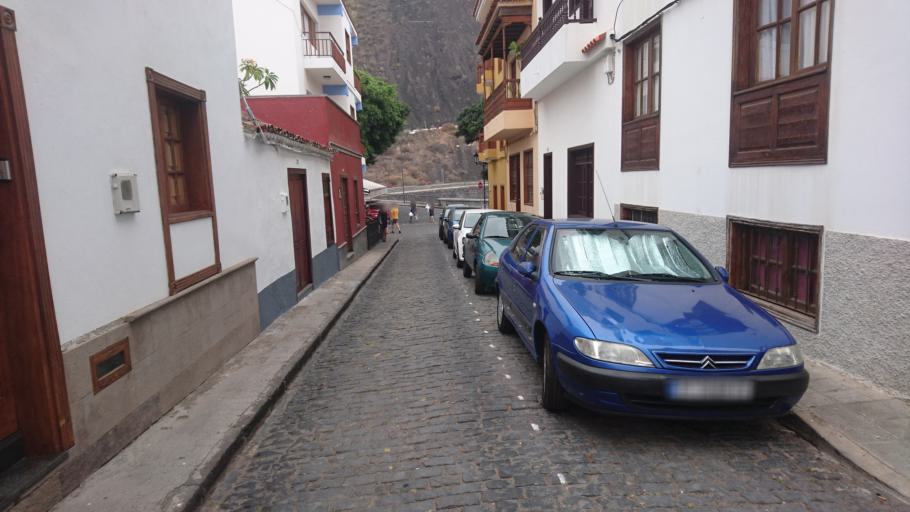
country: ES
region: Canary Islands
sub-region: Provincia de Santa Cruz de Tenerife
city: Garachico
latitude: 28.3716
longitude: -16.7673
